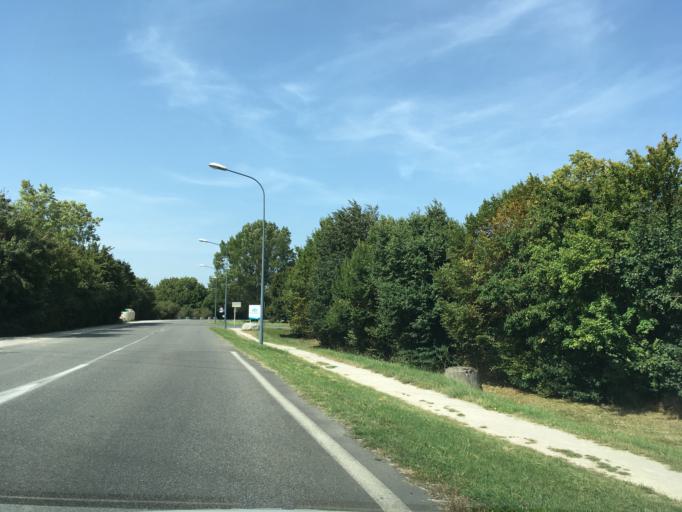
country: FR
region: Midi-Pyrenees
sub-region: Departement du Tarn
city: Castres
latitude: 43.6231
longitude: 2.2597
